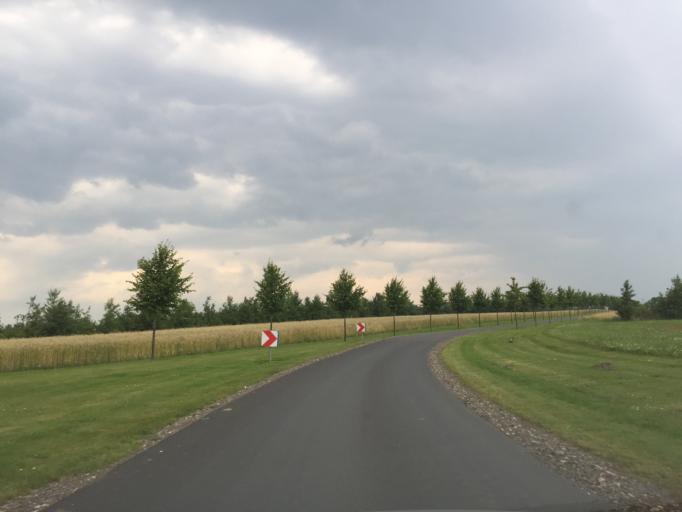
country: DK
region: Central Jutland
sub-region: Viborg Kommune
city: Bjerringbro
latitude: 56.3304
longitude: 9.6437
